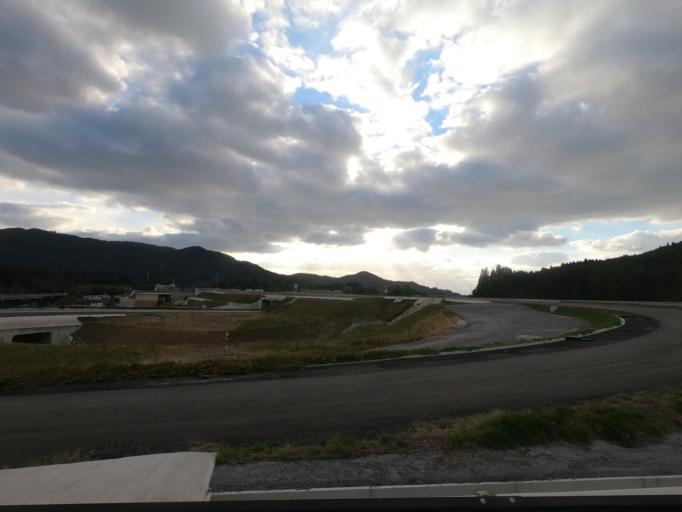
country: JP
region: Kumamoto
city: Minamata
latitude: 32.2118
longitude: 130.4260
